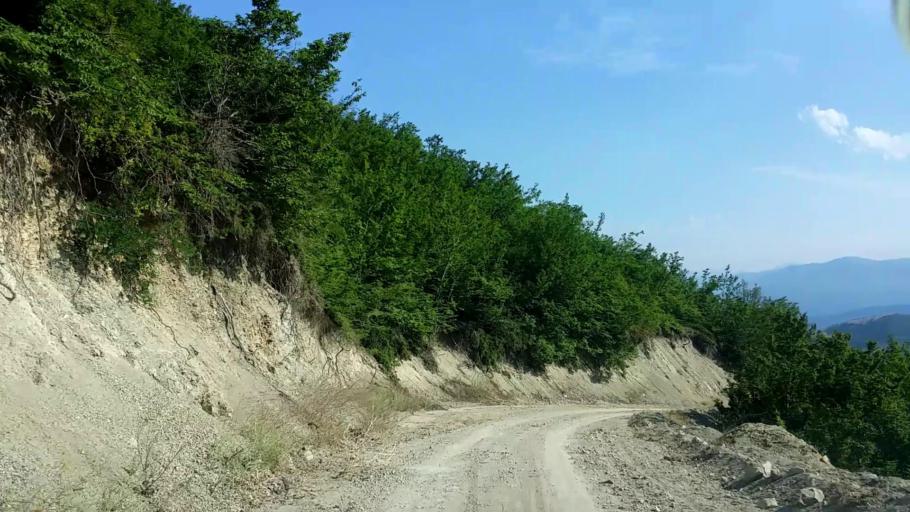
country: IR
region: Mazandaran
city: Chalus
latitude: 36.5521
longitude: 51.2949
